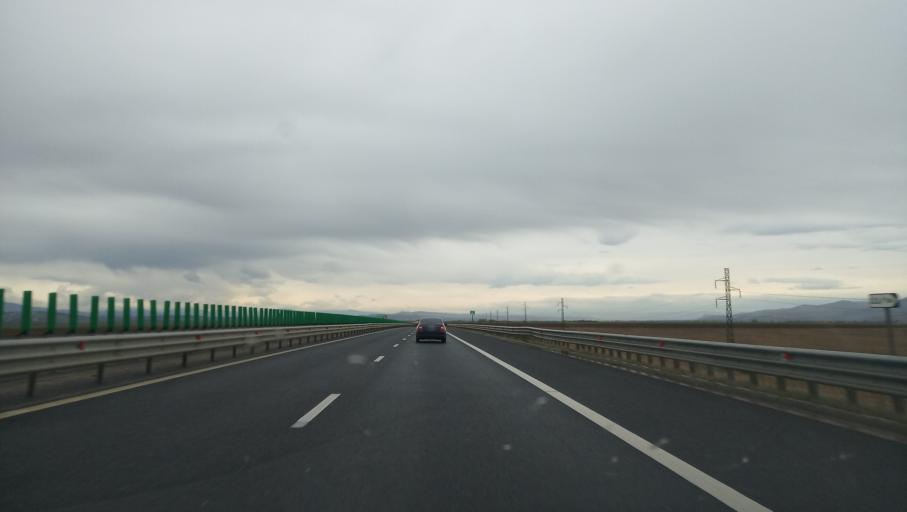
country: RO
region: Alba
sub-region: Comuna Sibot
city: Sibot
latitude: 45.9160
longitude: 23.3263
